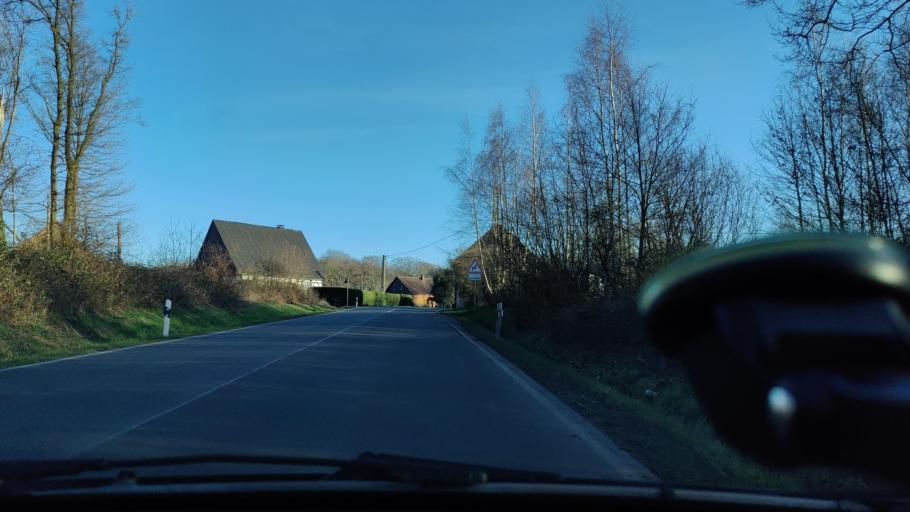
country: DE
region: North Rhine-Westphalia
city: Castrop-Rauxel
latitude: 51.5635
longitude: 7.2872
